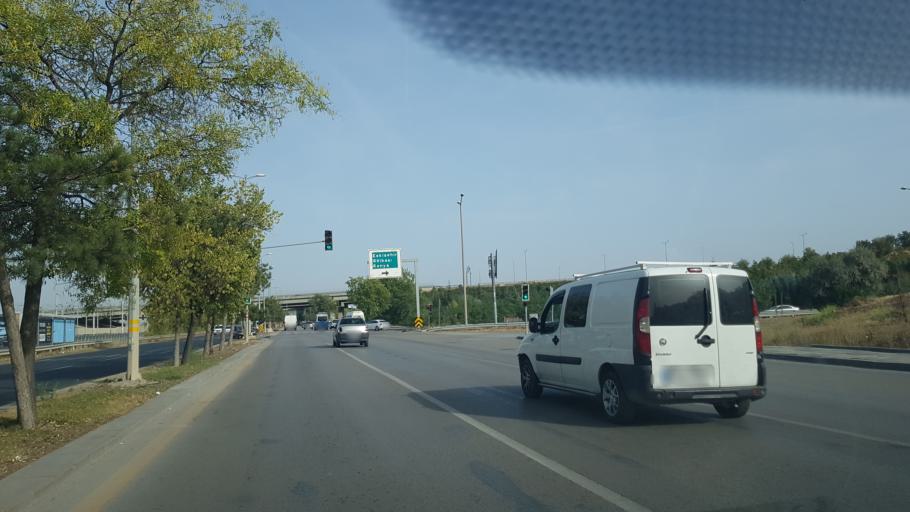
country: TR
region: Ankara
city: Etimesgut
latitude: 39.9564
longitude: 32.6202
